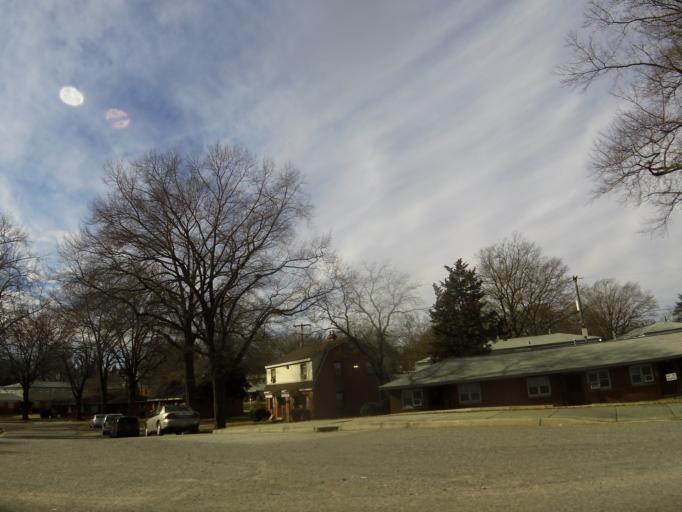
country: US
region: Virginia
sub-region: City of Hopewell
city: Hopewell
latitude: 37.2998
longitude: -77.2925
